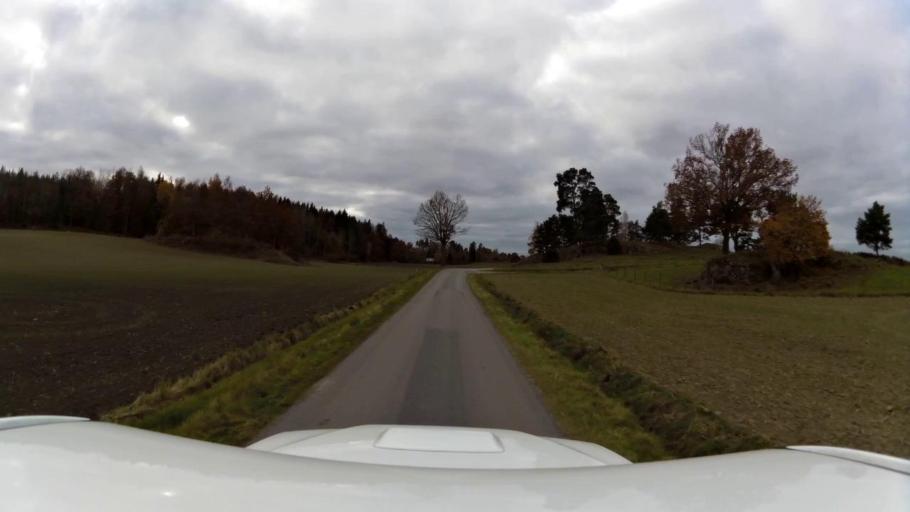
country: SE
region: OEstergoetland
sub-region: Linkopings Kommun
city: Linghem
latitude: 58.3841
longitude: 15.8340
